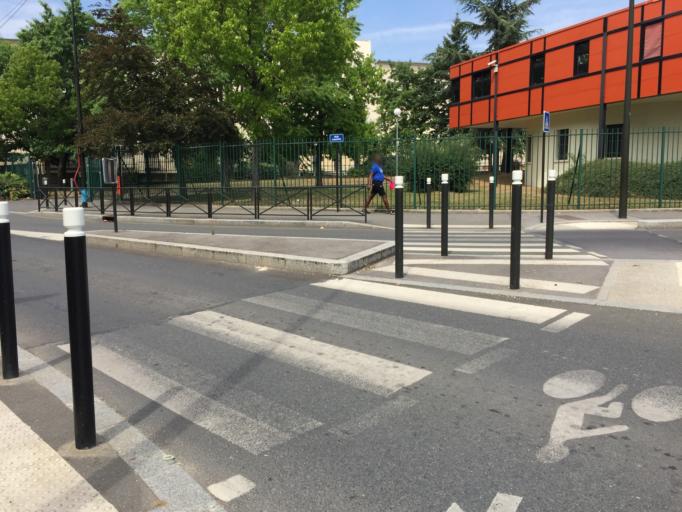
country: FR
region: Ile-de-France
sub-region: Departement de Seine-et-Marne
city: Nanteuil-les-Meaux
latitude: 48.9518
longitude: 2.9011
